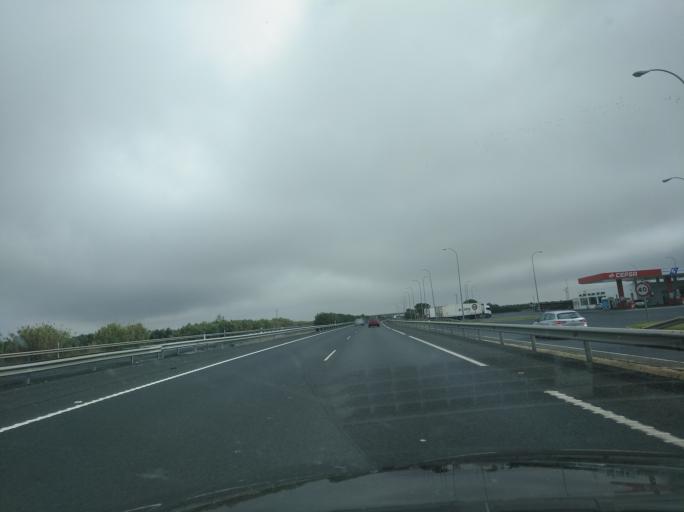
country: ES
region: Andalusia
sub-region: Provincia de Huelva
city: San Juan del Puerto
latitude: 37.3320
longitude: -6.8042
